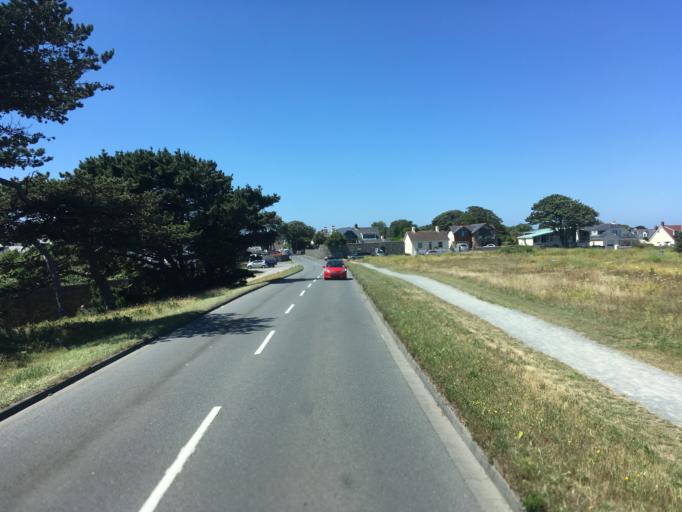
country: GG
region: St Peter Port
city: Saint Peter Port
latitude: 49.4908
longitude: -2.5452
